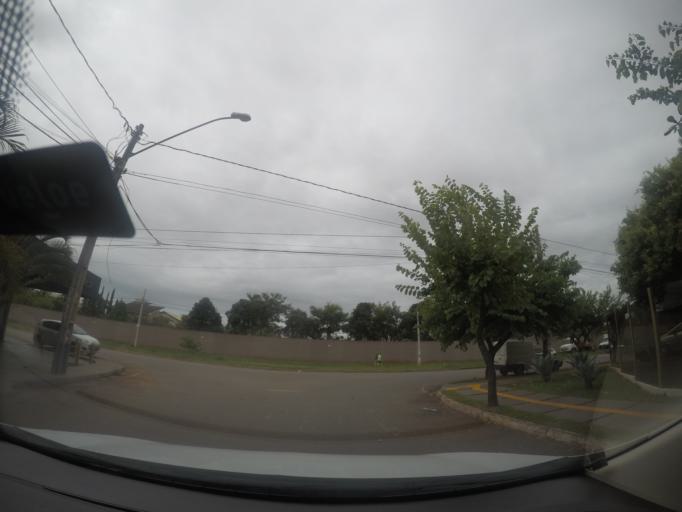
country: BR
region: Goias
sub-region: Goiania
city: Goiania
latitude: -16.7111
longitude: -49.3263
